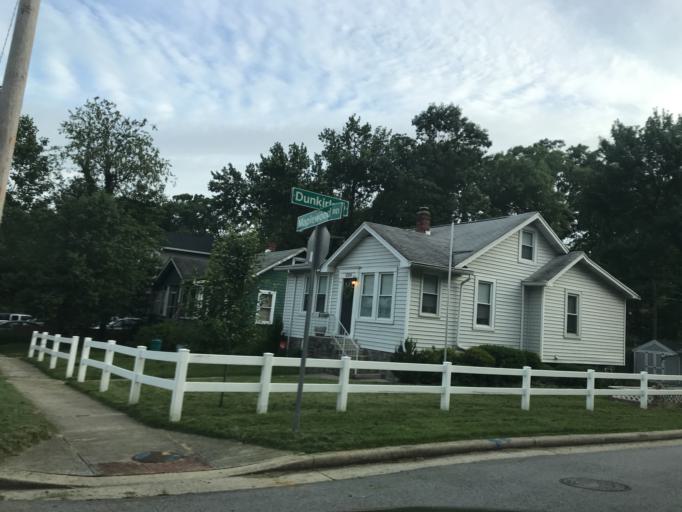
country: US
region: Maryland
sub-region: Baltimore County
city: Towson
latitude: 39.3755
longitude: -76.5982
